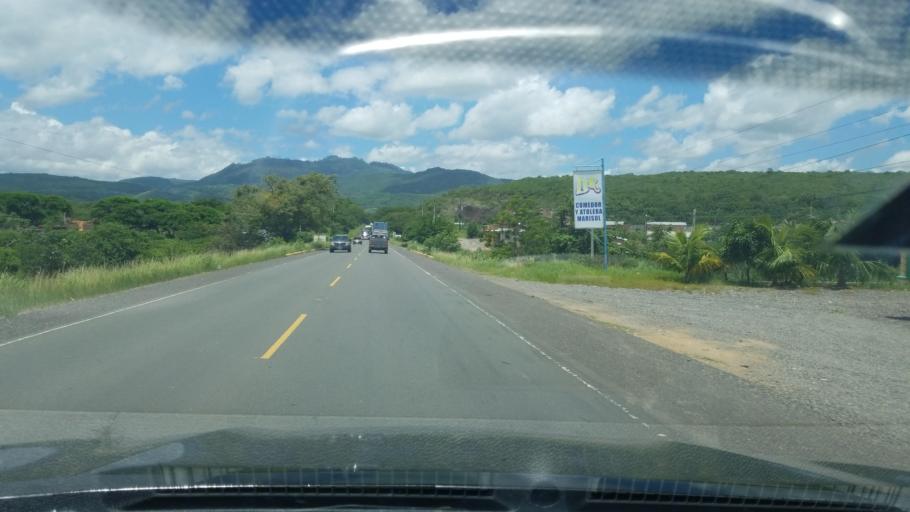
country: HN
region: Francisco Morazan
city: Cofradia
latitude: 14.2768
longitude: -87.2436
